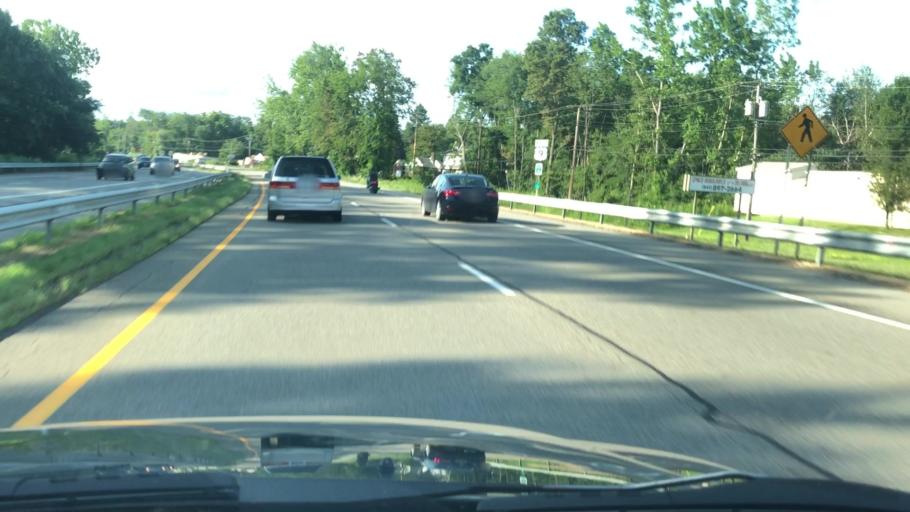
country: US
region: New York
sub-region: Dutchess County
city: Fishkill
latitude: 41.5589
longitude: -73.9034
